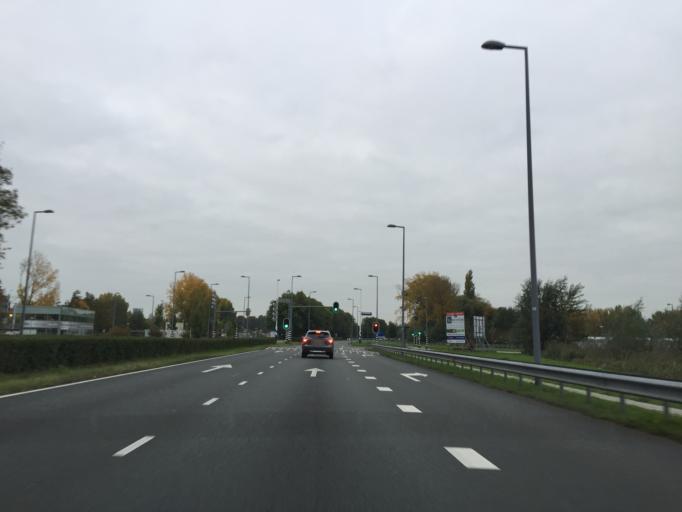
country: NL
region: South Holland
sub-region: Gemeente Rotterdam
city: Rotterdam
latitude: 51.9570
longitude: 4.4615
